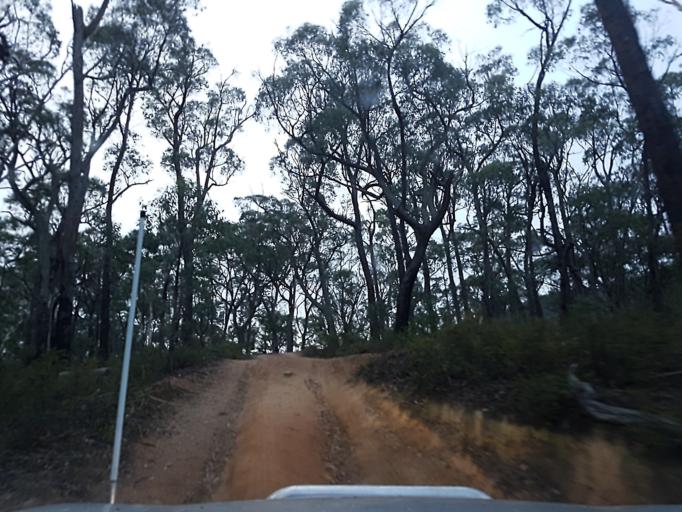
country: AU
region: New South Wales
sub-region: Snowy River
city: Jindabyne
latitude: -36.8640
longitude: 148.2370
